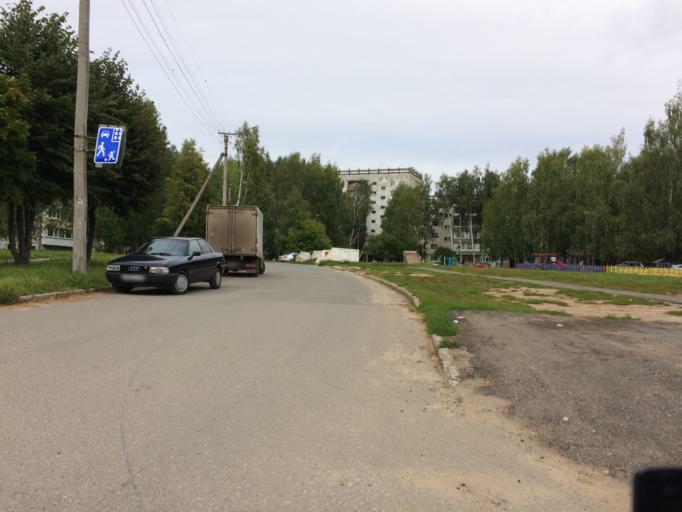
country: RU
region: Mariy-El
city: Yoshkar-Ola
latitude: 56.6491
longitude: 47.9698
